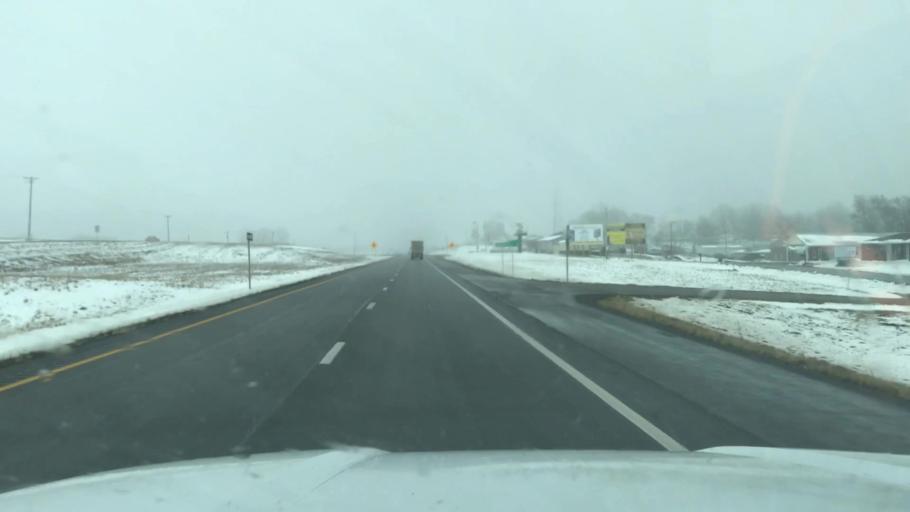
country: US
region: Missouri
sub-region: Clinton County
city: Gower
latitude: 39.7620
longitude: -94.5019
